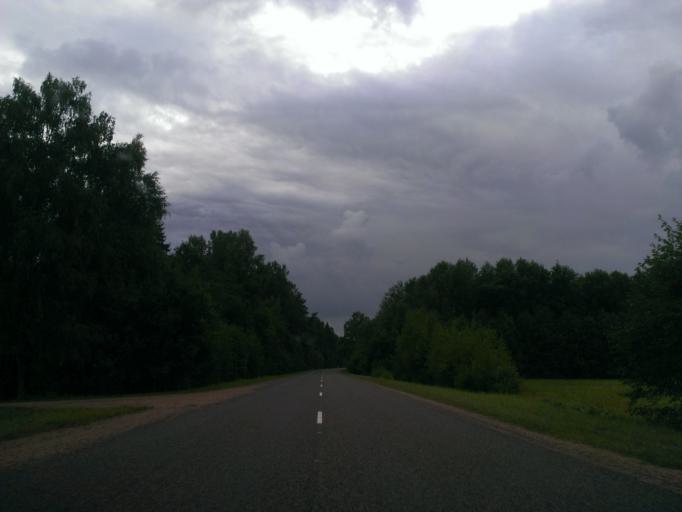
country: LV
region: Kegums
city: Kegums
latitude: 56.7583
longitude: 24.7442
